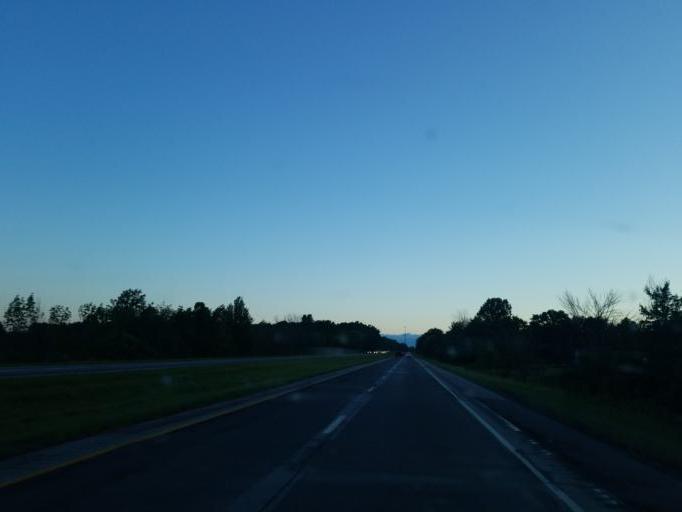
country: US
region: Ohio
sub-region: Wayne County
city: Doylestown
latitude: 40.9763
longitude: -81.6620
